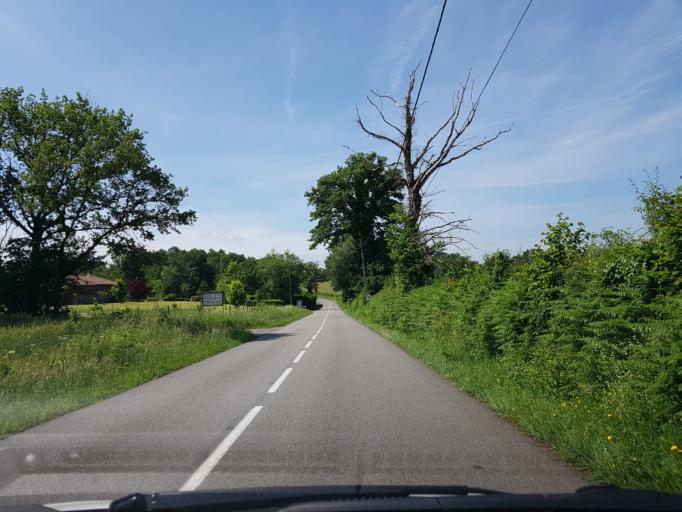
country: FR
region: Poitou-Charentes
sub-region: Departement de la Charente
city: Etagnac
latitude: 45.9196
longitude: 0.7427
